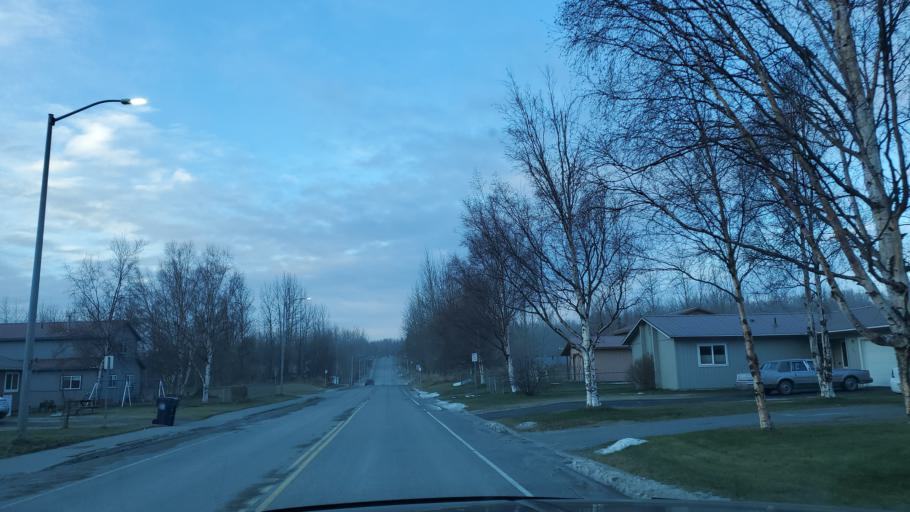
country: US
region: Alaska
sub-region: Matanuska-Susitna Borough
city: Palmer
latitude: 61.6139
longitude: -149.1050
